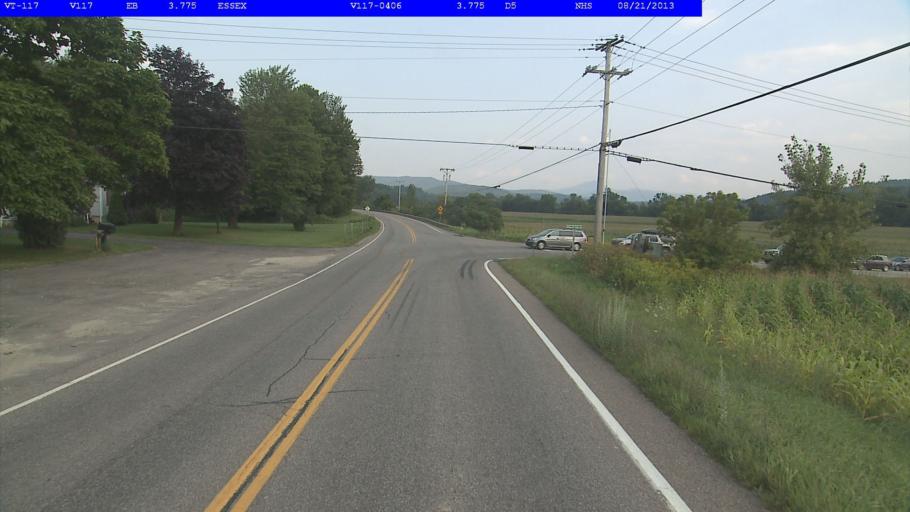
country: US
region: Vermont
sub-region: Chittenden County
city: Williston
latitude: 44.4755
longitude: -73.0416
